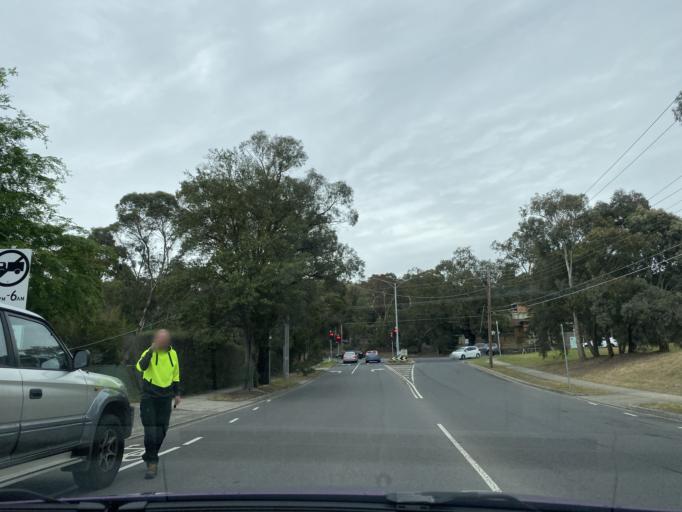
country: AU
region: Victoria
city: Saint Helena
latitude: -37.7040
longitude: 145.1284
